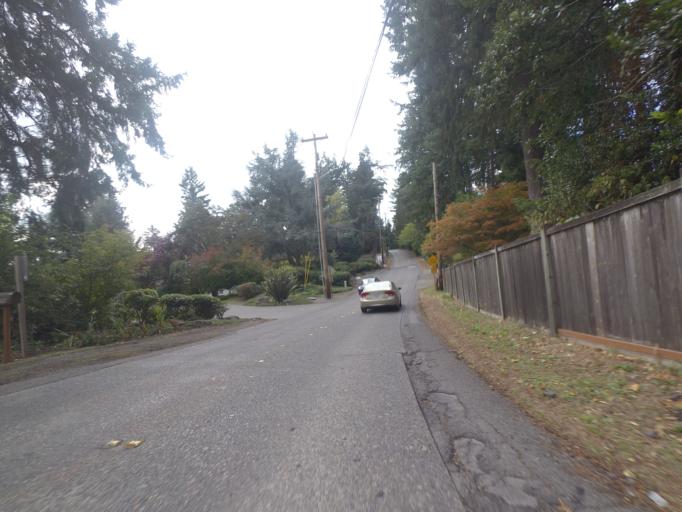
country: US
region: Washington
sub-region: Pierce County
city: Lakewood
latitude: 47.1672
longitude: -122.5339
